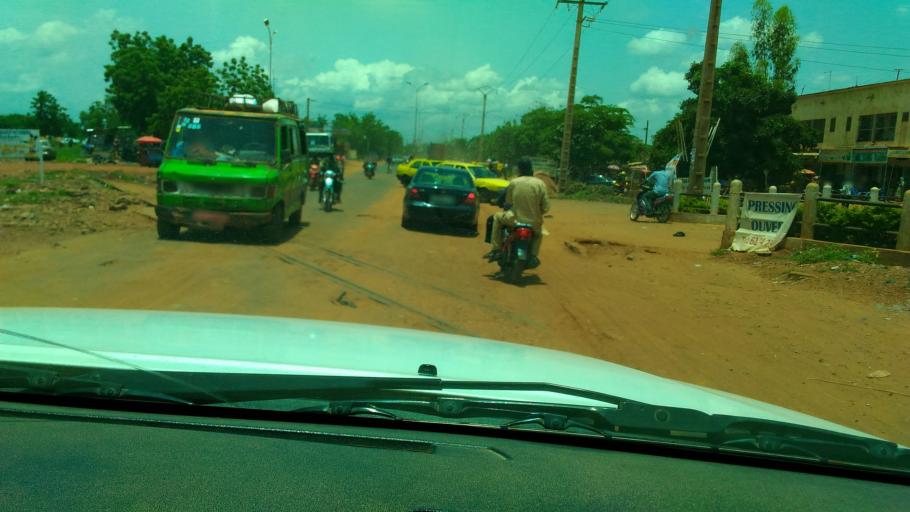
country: ML
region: Bamako
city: Bamako
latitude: 12.6700
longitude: -7.9175
